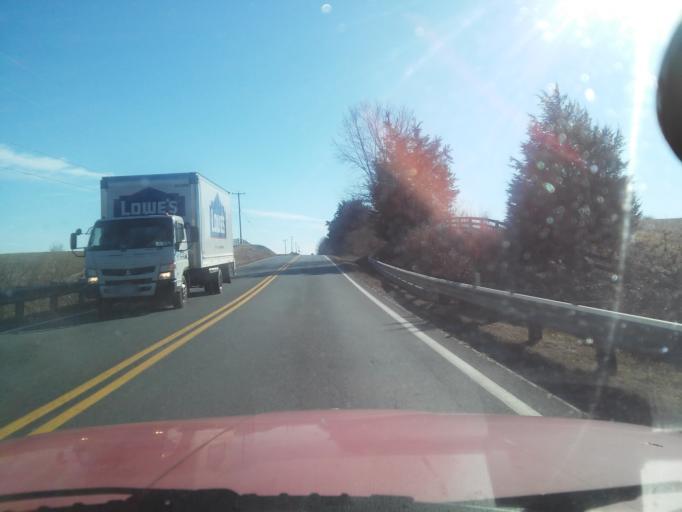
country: US
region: Virginia
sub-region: Orange County
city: Gordonsville
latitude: 38.0462
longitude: -78.1890
